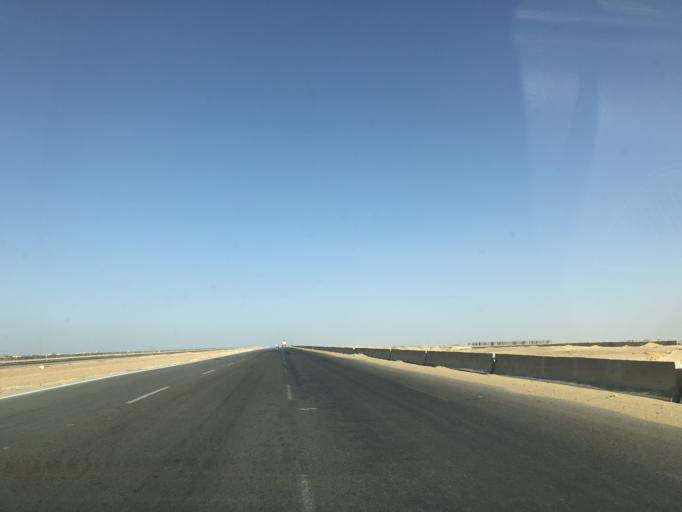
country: EG
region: Muhafazat al Minufiyah
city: Ashmun
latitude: 30.0675
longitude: 30.8622
